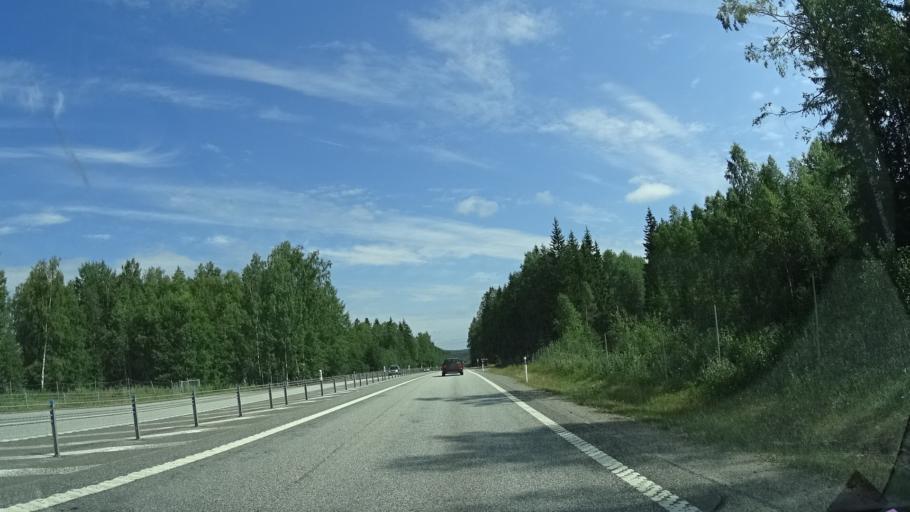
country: SE
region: Vaermland
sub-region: Kristinehamns Kommun
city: Bjorneborg
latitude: 59.3180
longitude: 14.3397
